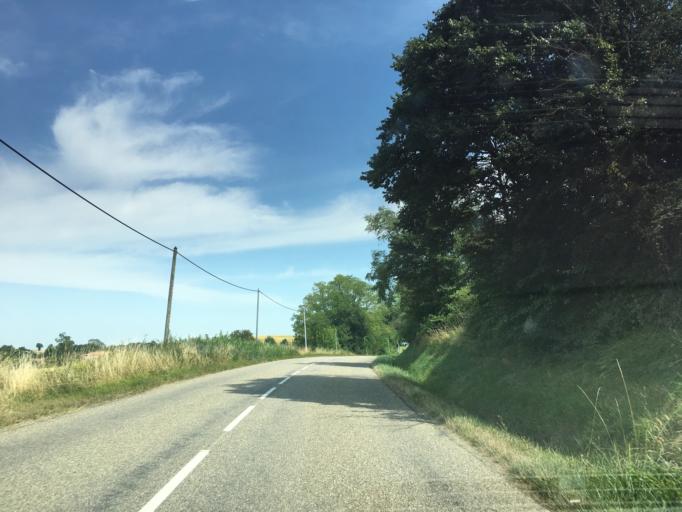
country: FR
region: Midi-Pyrenees
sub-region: Departement du Gers
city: Fleurance
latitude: 43.8636
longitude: 0.7153
